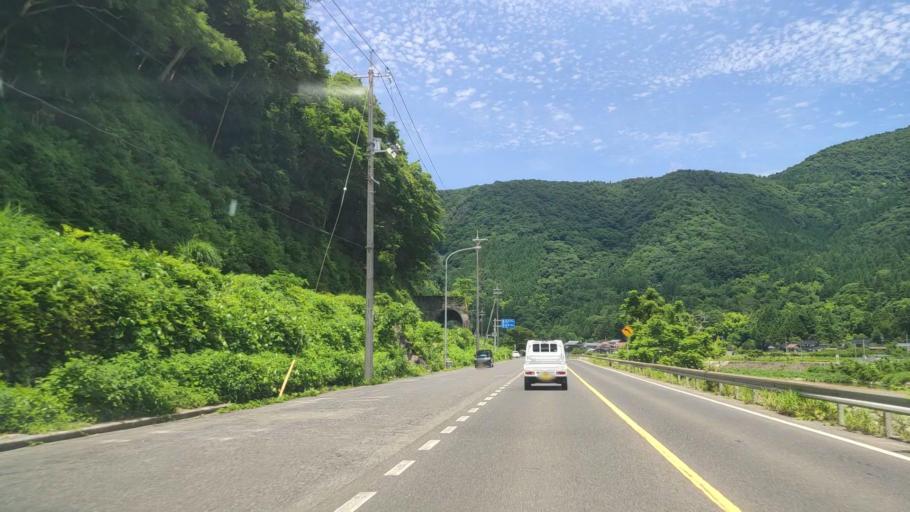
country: JP
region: Tottori
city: Tottori
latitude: 35.3644
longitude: 134.3780
